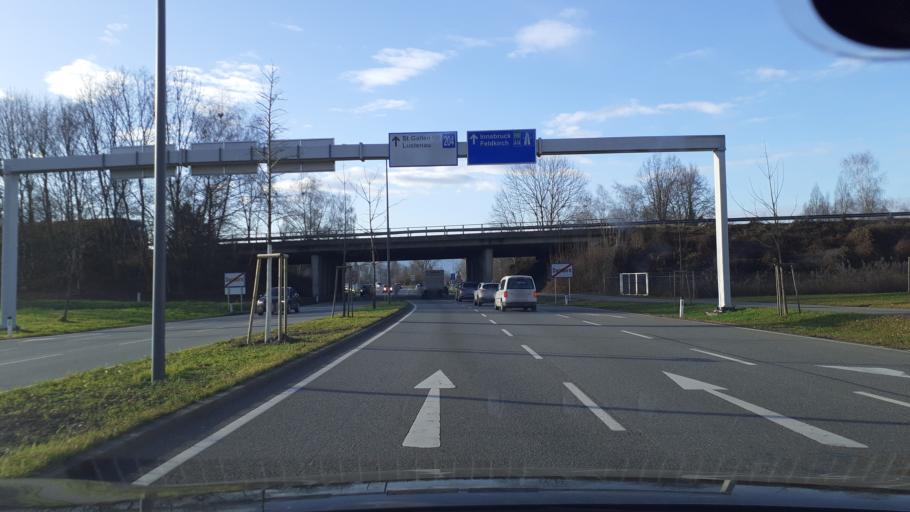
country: AT
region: Vorarlberg
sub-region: Politischer Bezirk Dornbirn
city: Dornbirn
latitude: 47.4134
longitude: 9.7093
